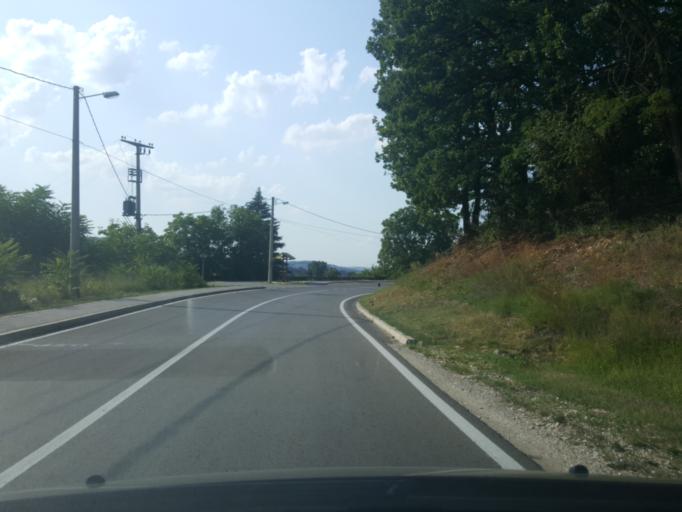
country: RS
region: Central Serbia
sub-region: Sumadijski Okrug
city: Topola
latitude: 44.2407
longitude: 20.6772
